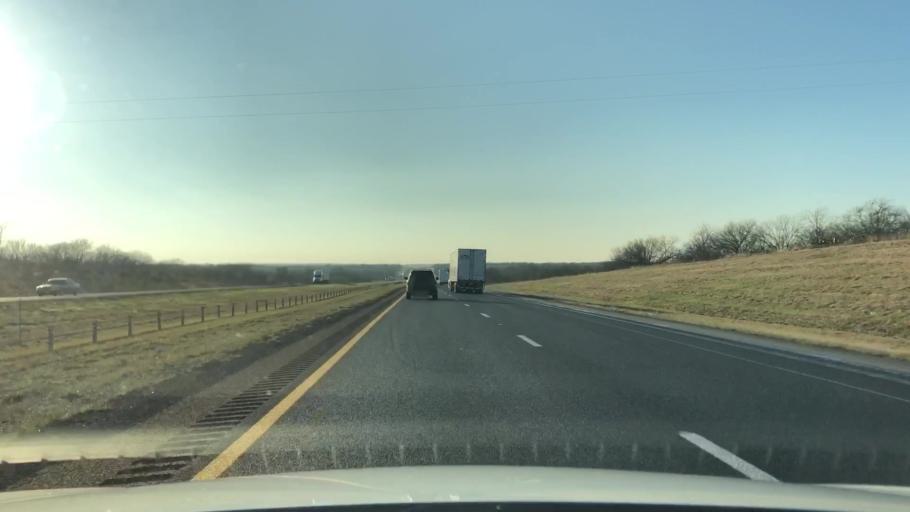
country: US
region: Texas
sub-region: Gonzales County
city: Waelder
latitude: 29.6668
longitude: -97.3344
